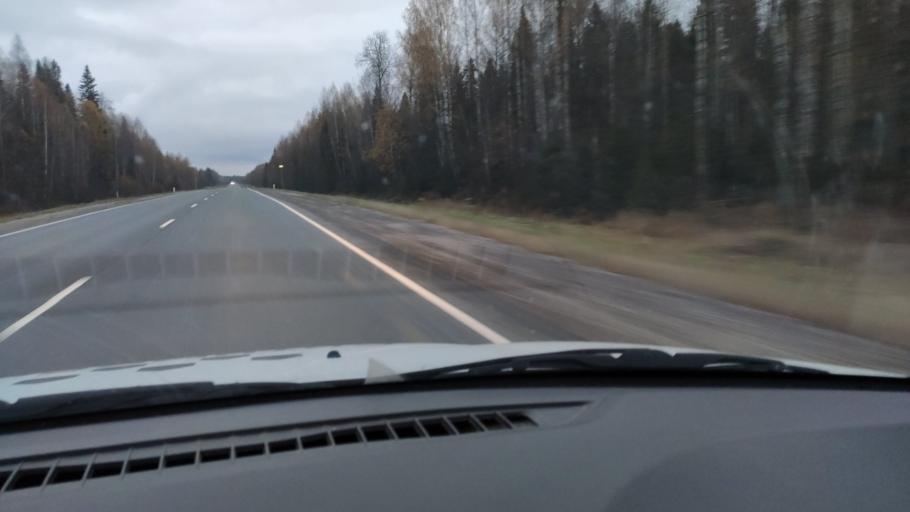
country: RU
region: Kirov
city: Kostino
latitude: 58.8450
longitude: 53.0812
